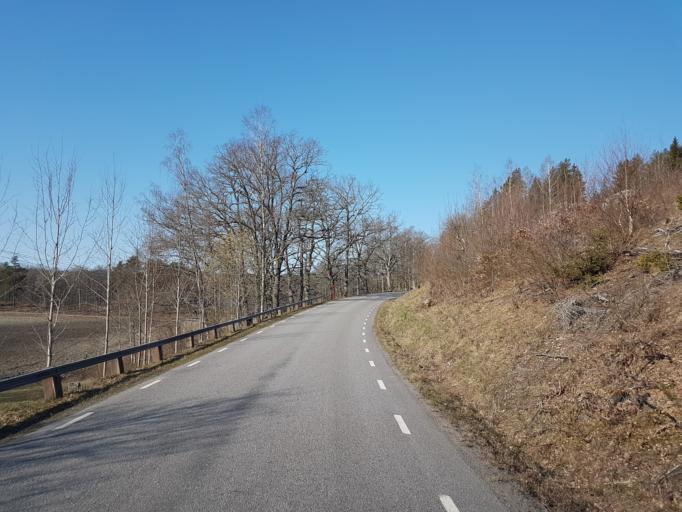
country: SE
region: OEstergoetland
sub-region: Valdemarsviks Kommun
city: Gusum
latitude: 58.1948
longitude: 16.3302
